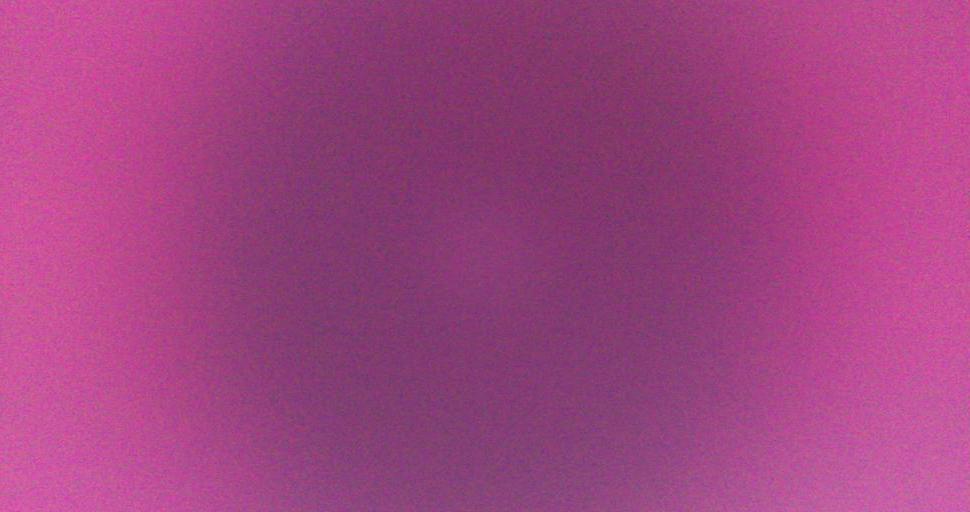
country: ME
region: Herceg Novi
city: Herceg-Novi
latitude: 42.4520
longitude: 18.5345
